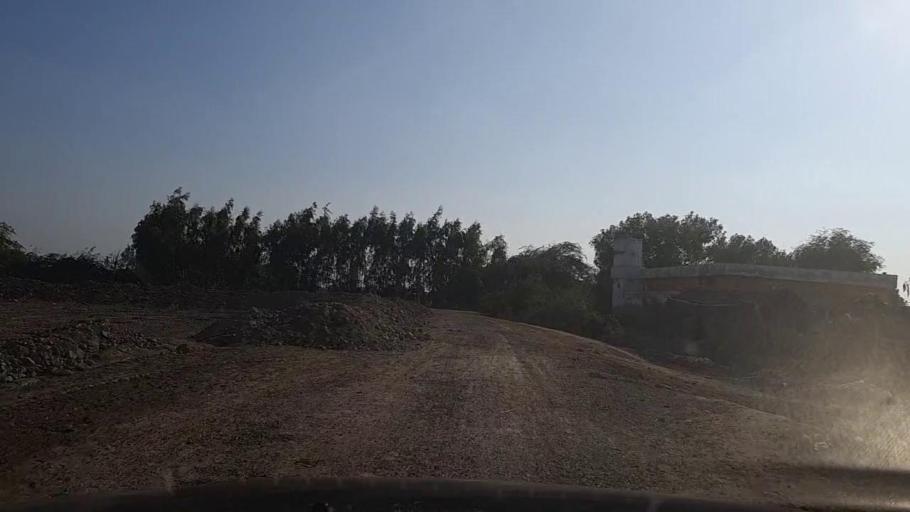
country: PK
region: Sindh
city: Gharo
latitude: 24.7044
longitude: 67.7045
